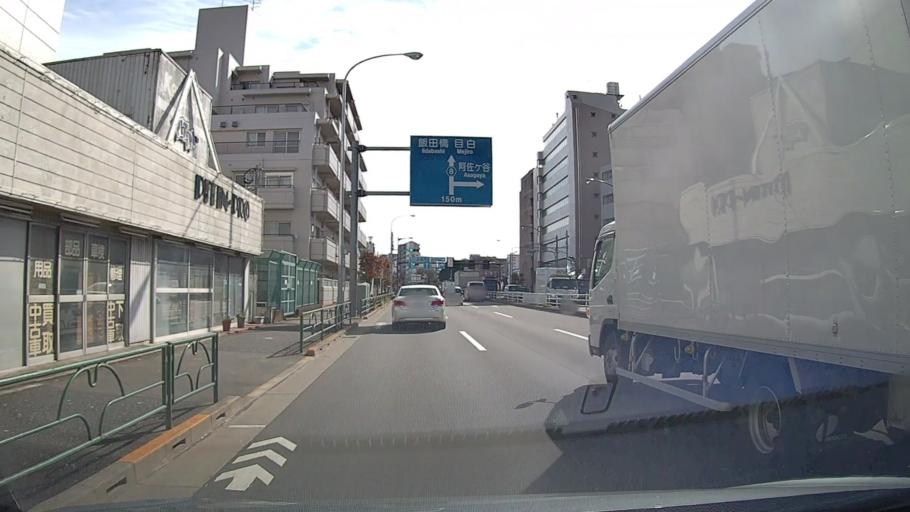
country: JP
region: Saitama
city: Wako
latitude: 35.7408
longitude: 139.6367
